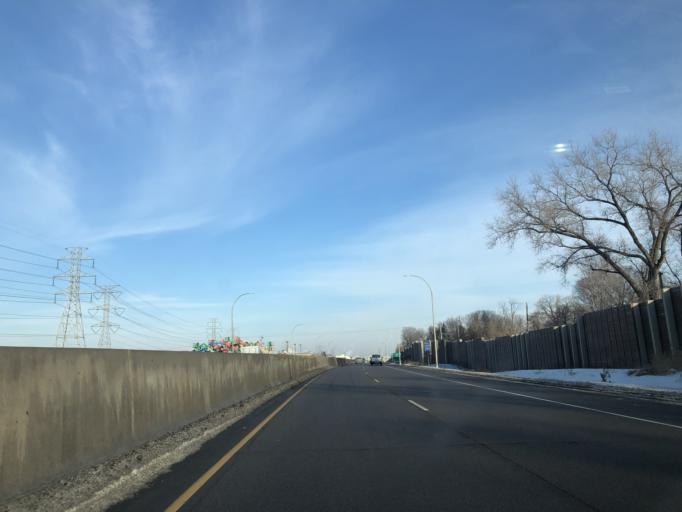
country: US
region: Minnesota
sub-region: Ramsey County
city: Lauderdale
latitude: 44.9955
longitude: -93.2060
